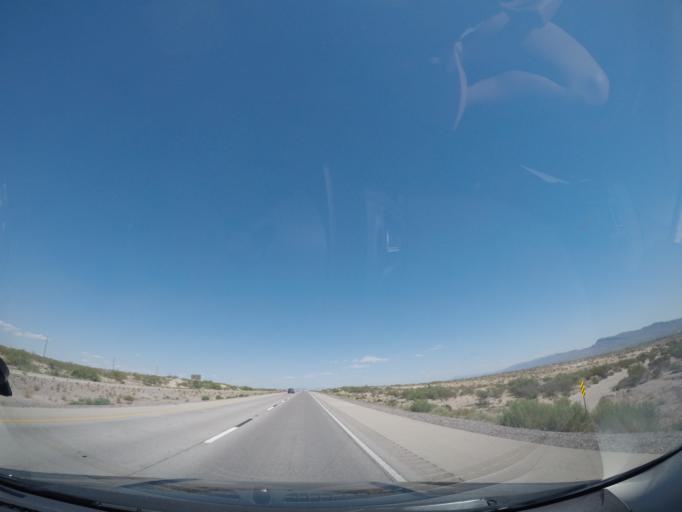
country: MX
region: Chihuahua
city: Praxedis Guerrero
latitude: 31.4182
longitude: -105.9900
